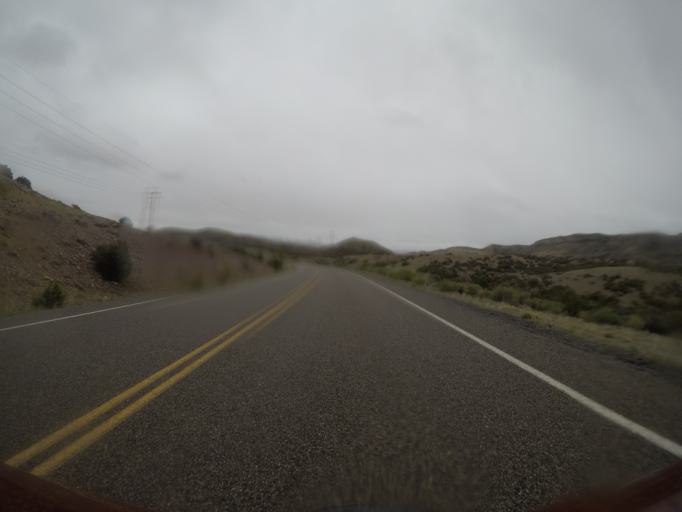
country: US
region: Wyoming
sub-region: Big Horn County
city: Lovell
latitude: 45.0229
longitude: -108.2698
